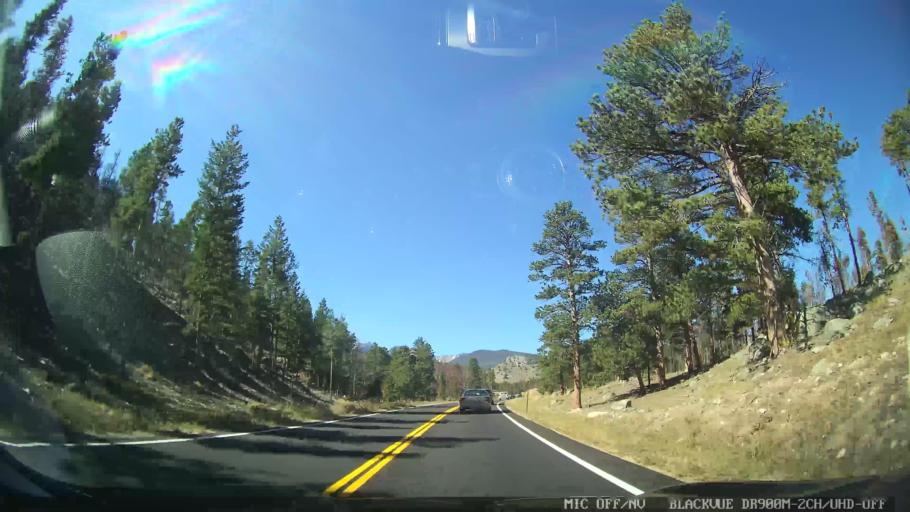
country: US
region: Colorado
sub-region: Larimer County
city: Estes Park
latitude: 40.3402
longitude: -105.5969
